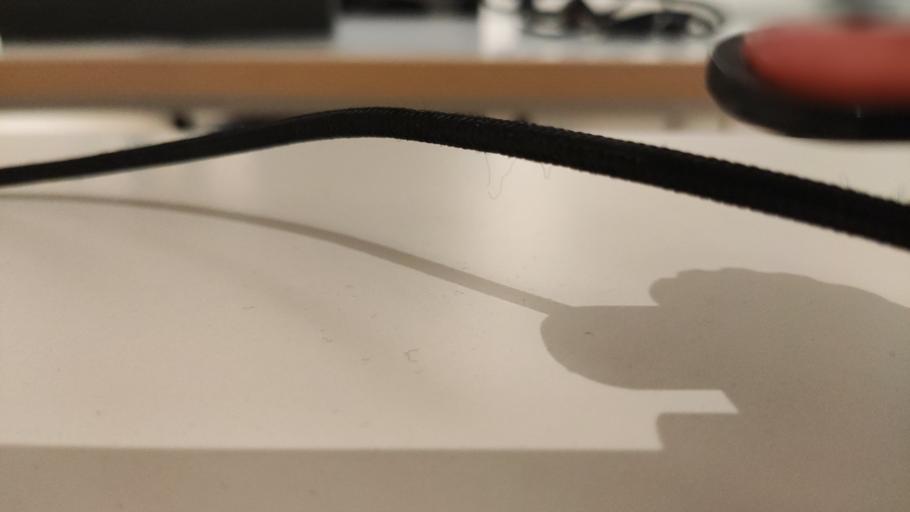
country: RU
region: Moskovskaya
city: Dorokhovo
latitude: 55.5180
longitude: 36.3530
